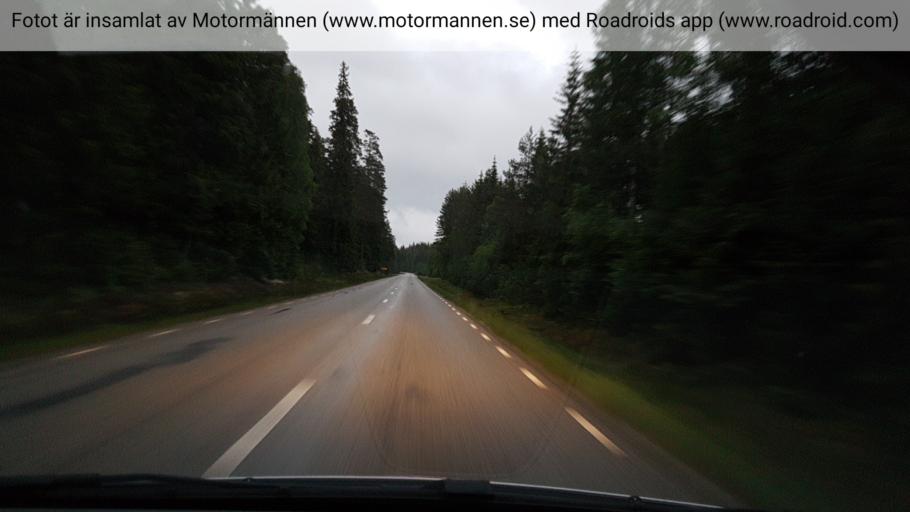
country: SE
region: Dalarna
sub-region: Smedjebackens Kommun
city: Smedjebacken
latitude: 59.9150
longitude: 15.4544
